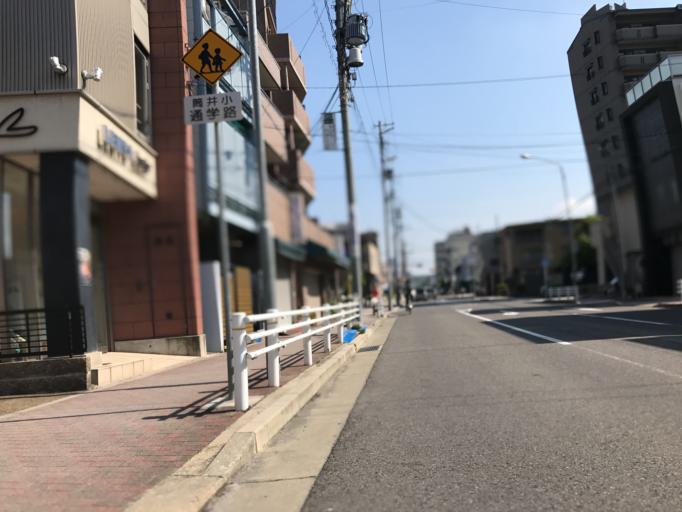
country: JP
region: Aichi
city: Nagoya-shi
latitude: 35.1757
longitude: 136.9289
